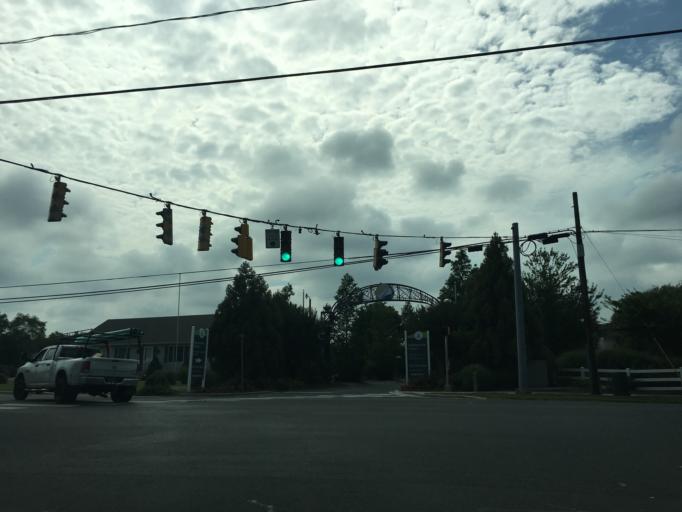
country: US
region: Delaware
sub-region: Sussex County
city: Ocean View
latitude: 38.5559
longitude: -75.0838
